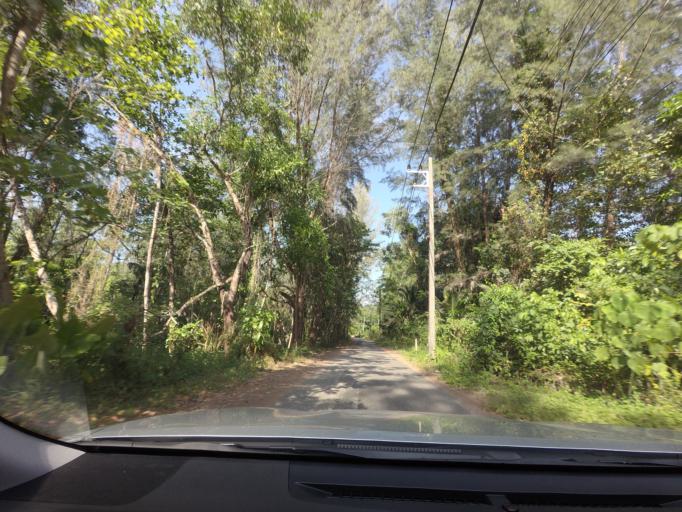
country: TH
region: Phangnga
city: Ban Khao Lak
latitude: 8.7384
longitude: 98.2449
